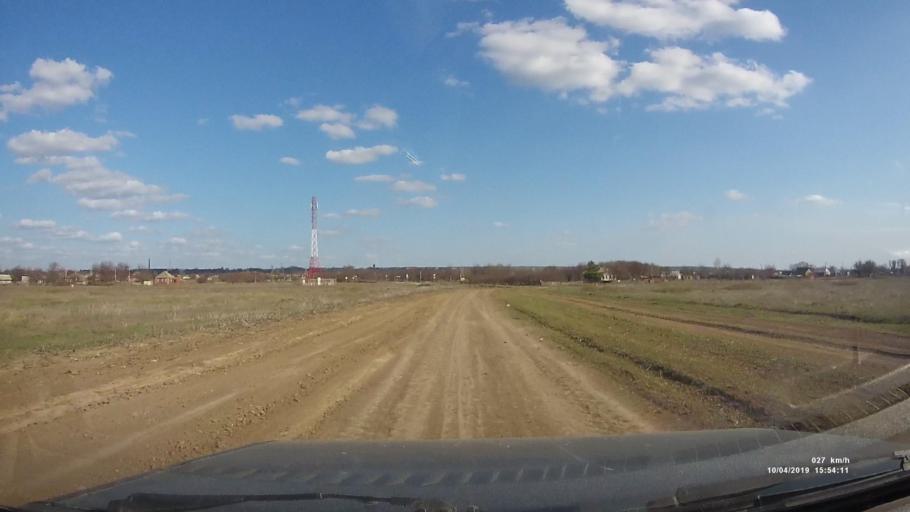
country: RU
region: Rostov
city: Masalovka
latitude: 48.4150
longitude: 40.2589
